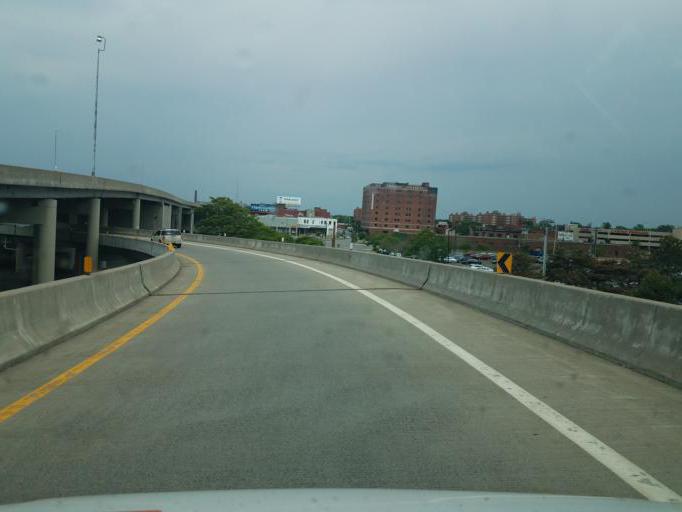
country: US
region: New York
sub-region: Erie County
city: Buffalo
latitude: 42.8768
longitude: -78.8729
